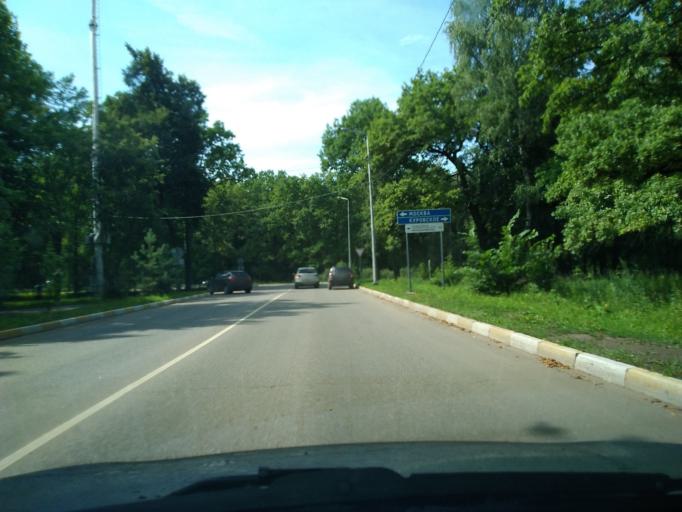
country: RU
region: Moskovskaya
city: Voskresensk
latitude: 55.3277
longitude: 38.6602
